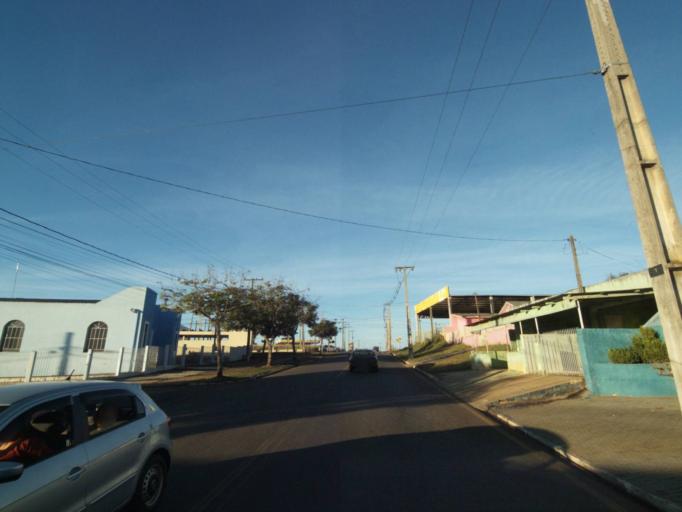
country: BR
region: Parana
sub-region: Tibagi
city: Tibagi
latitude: -24.5106
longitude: -50.4180
